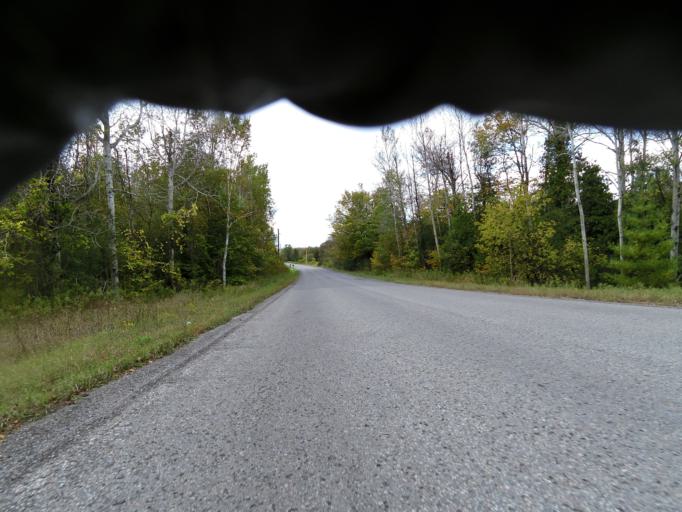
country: CA
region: Ontario
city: Cobourg
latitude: 43.9735
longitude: -78.0637
